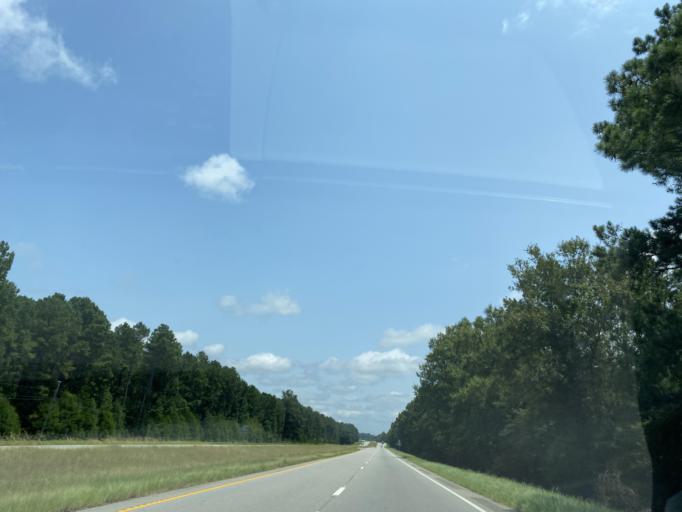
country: US
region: Georgia
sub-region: Telfair County
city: Lumber City
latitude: 31.9069
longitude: -82.6632
